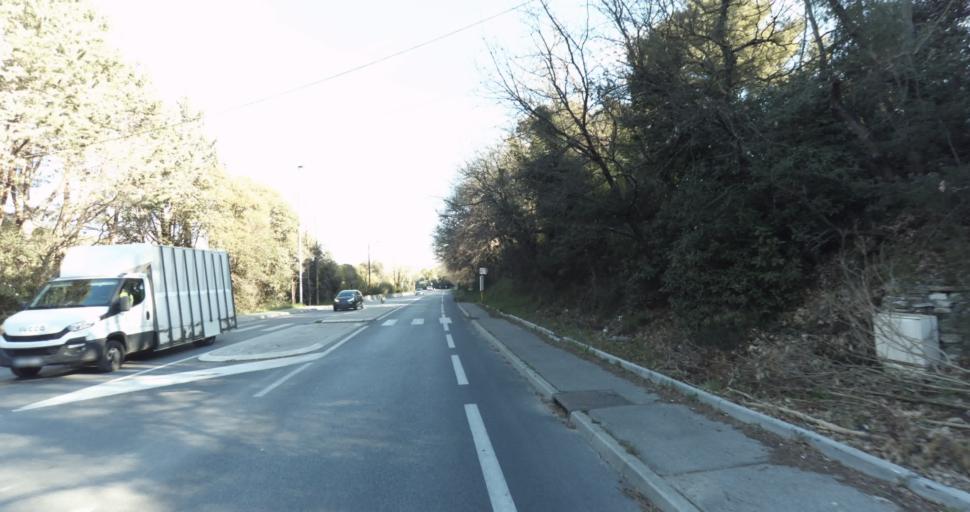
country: FR
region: Provence-Alpes-Cote d'Azur
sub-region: Departement des Bouches-du-Rhone
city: Aix-en-Provence
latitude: 43.5549
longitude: 5.4341
